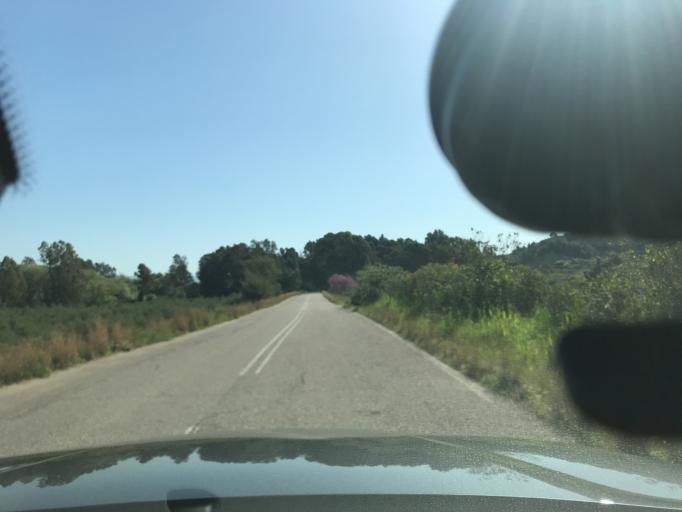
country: GR
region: West Greece
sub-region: Nomos Ileias
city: Epitalion
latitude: 37.6427
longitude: 21.5061
